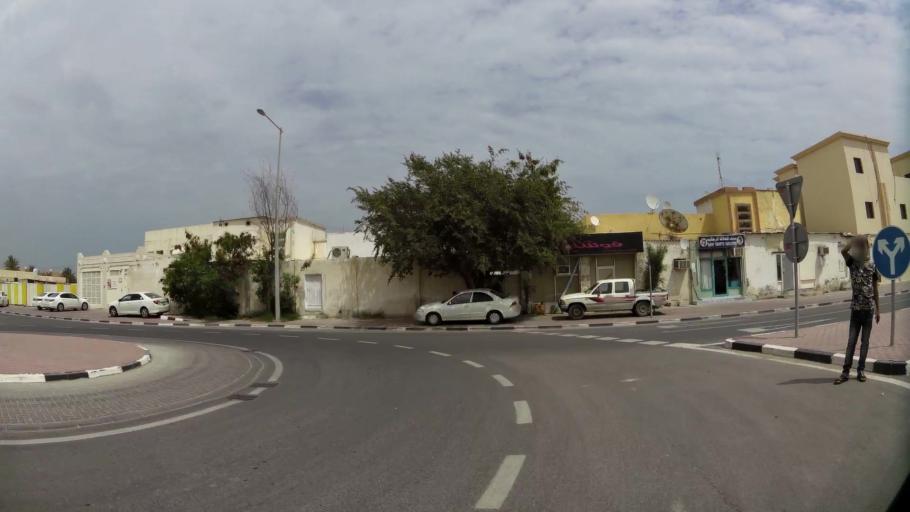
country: QA
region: Baladiyat ar Rayyan
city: Ar Rayyan
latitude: 25.3284
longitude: 51.4714
